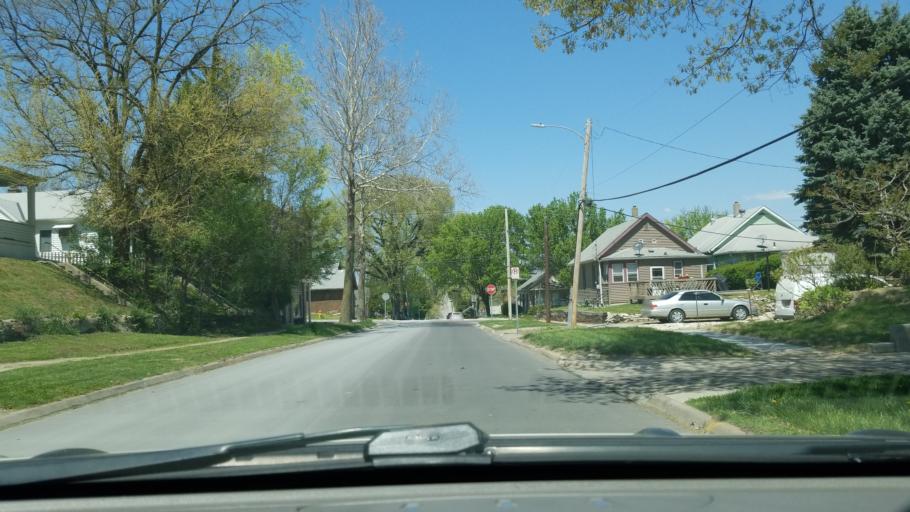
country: US
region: Nebraska
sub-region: Douglas County
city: Omaha
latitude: 41.2245
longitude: -95.9374
